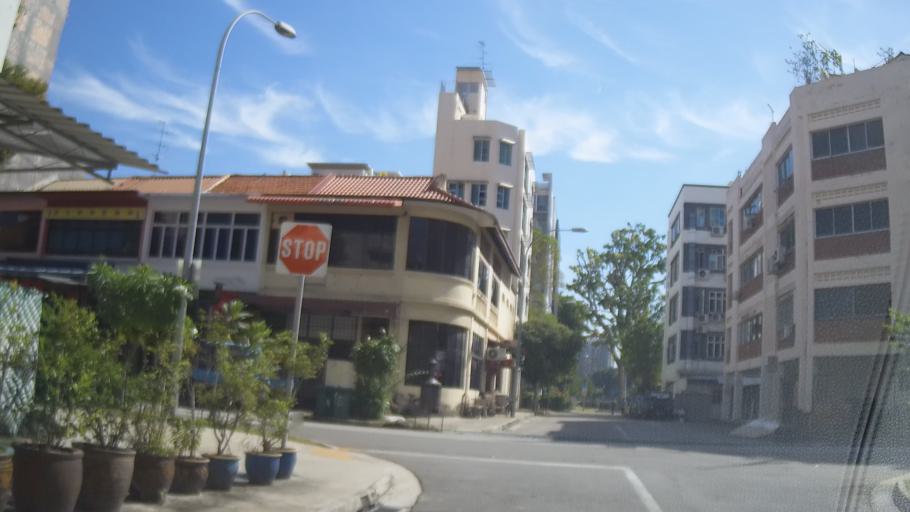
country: SG
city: Singapore
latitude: 1.3131
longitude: 103.8877
